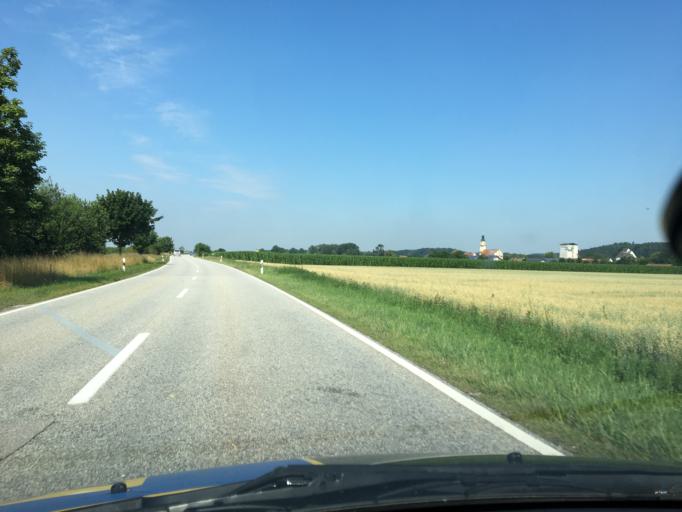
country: DE
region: Bavaria
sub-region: Upper Bavaria
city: Erharting
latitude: 48.2735
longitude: 12.5837
